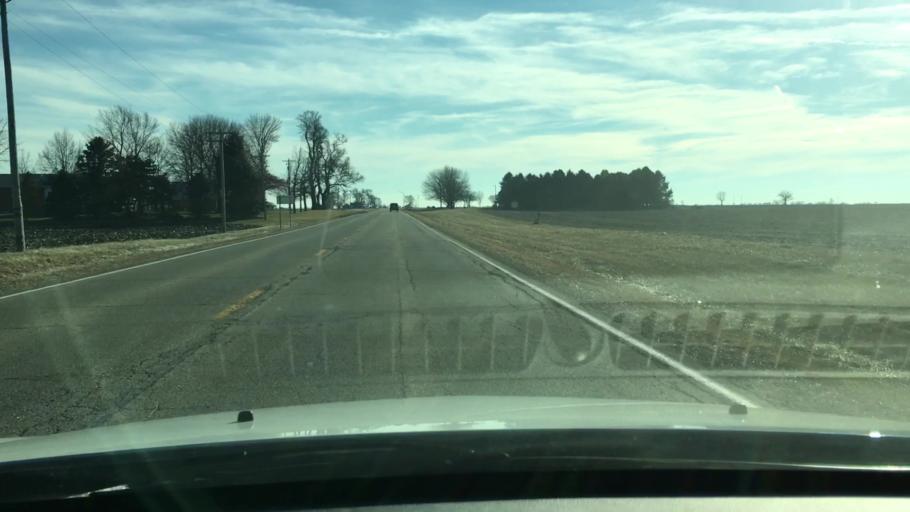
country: US
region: Illinois
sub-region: LaSalle County
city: Mendota
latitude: 41.4762
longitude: -89.1267
